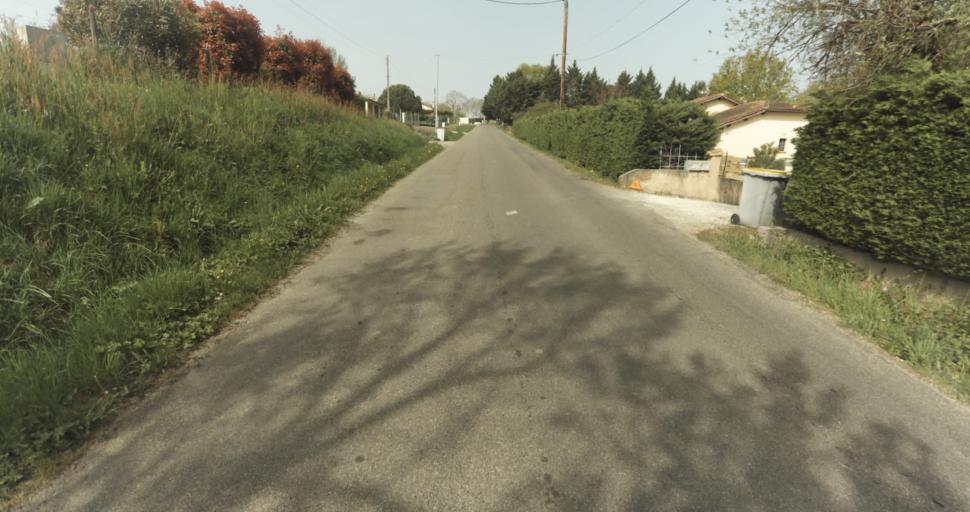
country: FR
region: Midi-Pyrenees
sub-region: Departement du Tarn-et-Garonne
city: Moissac
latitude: 44.1205
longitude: 1.0920
